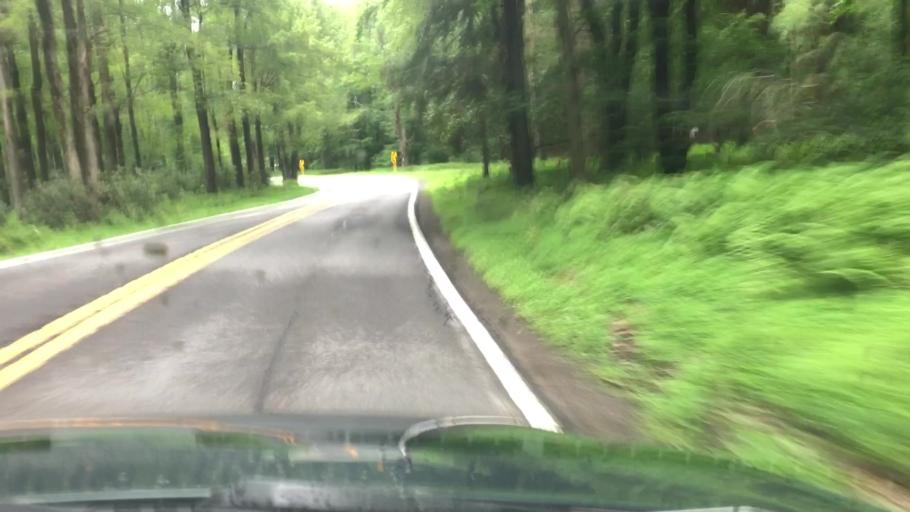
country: US
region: Pennsylvania
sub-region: Monroe County
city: Mountainhome
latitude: 41.3064
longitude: -75.2116
